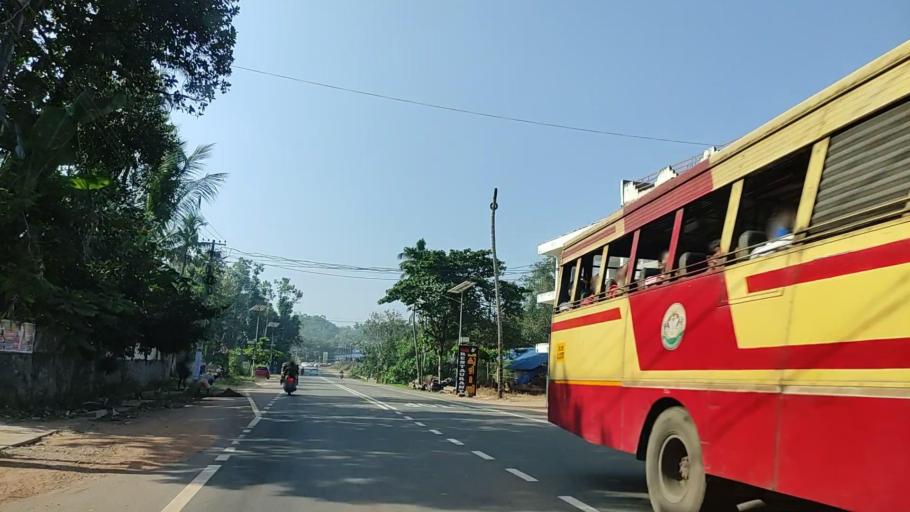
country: IN
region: Kerala
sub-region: Kollam
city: Punalur
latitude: 8.8806
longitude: 76.8674
